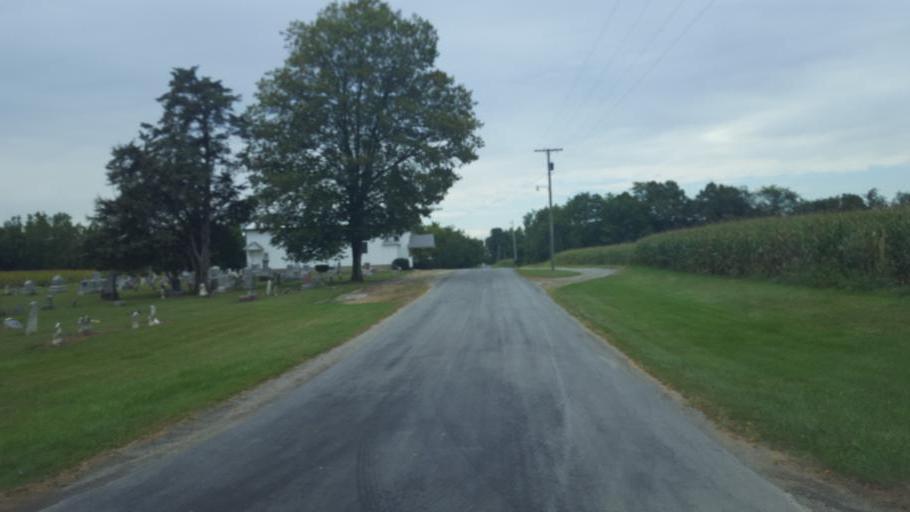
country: US
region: Ohio
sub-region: Wyandot County
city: Upper Sandusky
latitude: 40.8769
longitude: -83.1892
